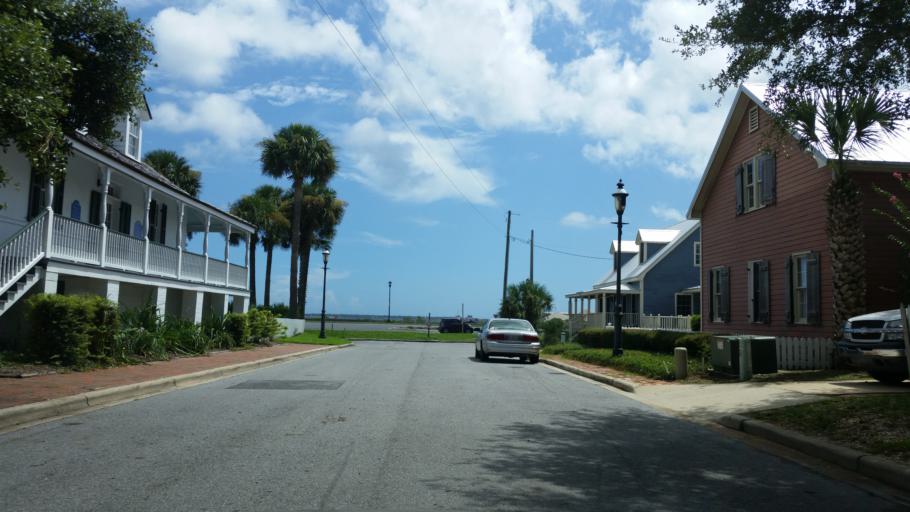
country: US
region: Florida
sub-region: Escambia County
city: Pensacola
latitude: 30.4092
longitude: -87.2074
